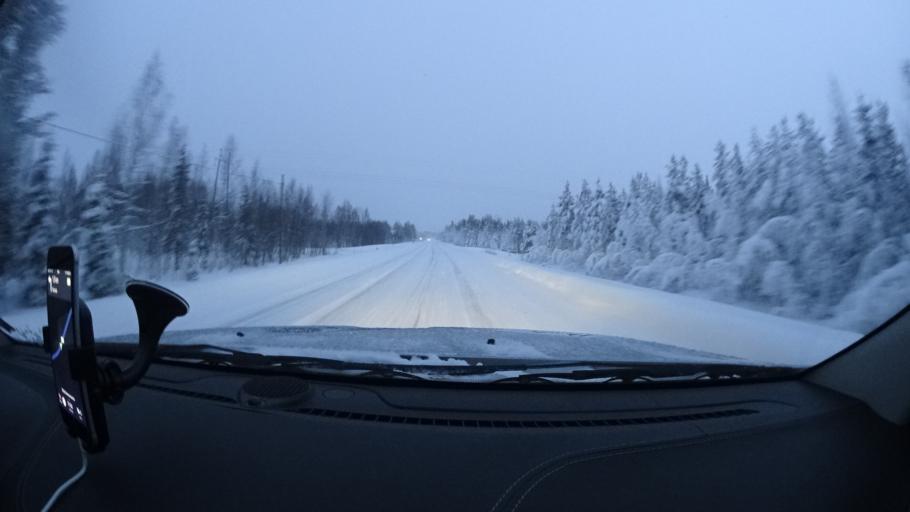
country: FI
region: Lapland
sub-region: Tunturi-Lappi
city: Kittilae
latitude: 67.6644
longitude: 24.8546
